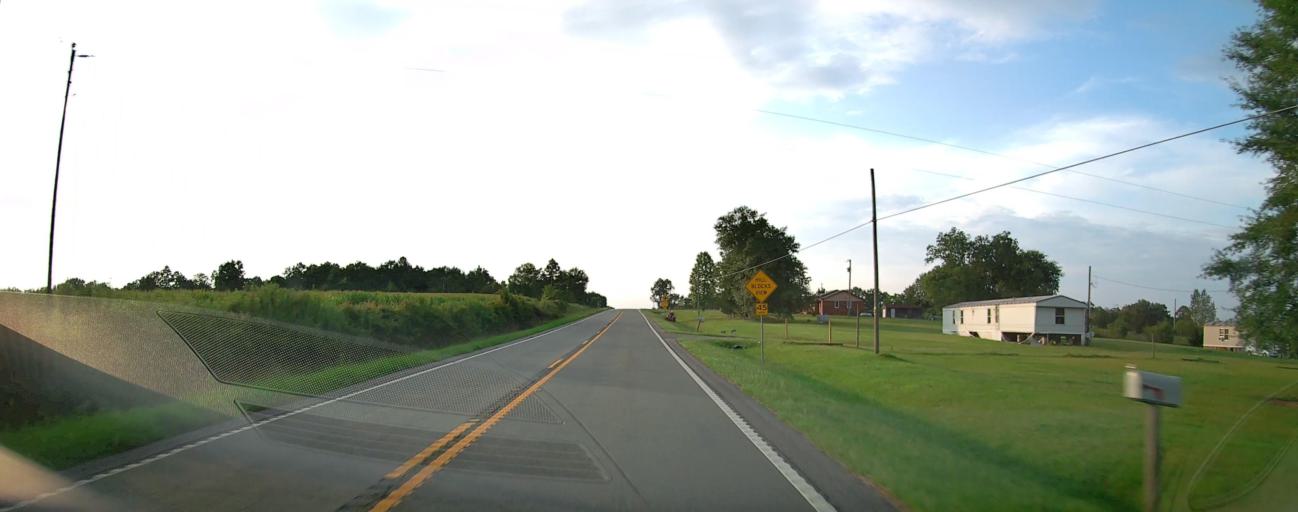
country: US
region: Georgia
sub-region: Taylor County
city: Reynolds
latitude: 32.5932
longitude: -84.0916
